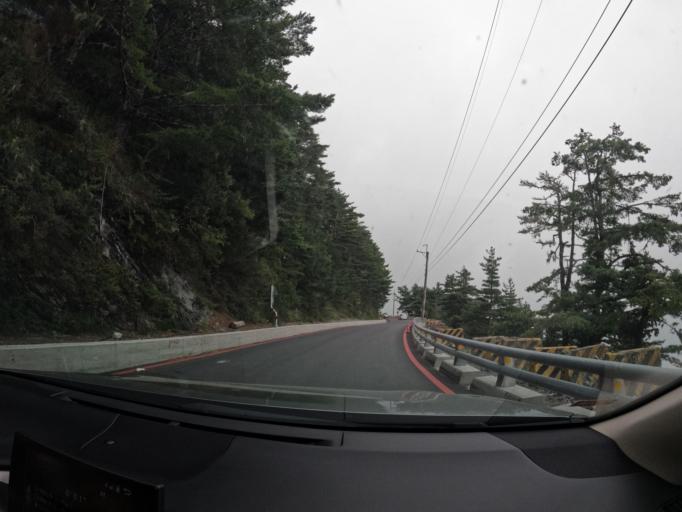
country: TW
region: Taiwan
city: Yujing
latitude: 23.2649
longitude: 120.9645
